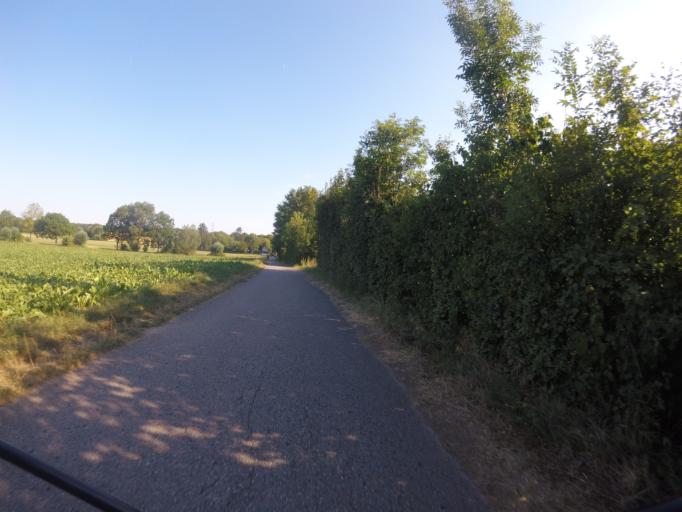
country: DE
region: Baden-Wuerttemberg
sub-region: Regierungsbezirk Stuttgart
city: Ludwigsburg
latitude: 48.9204
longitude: 9.1731
